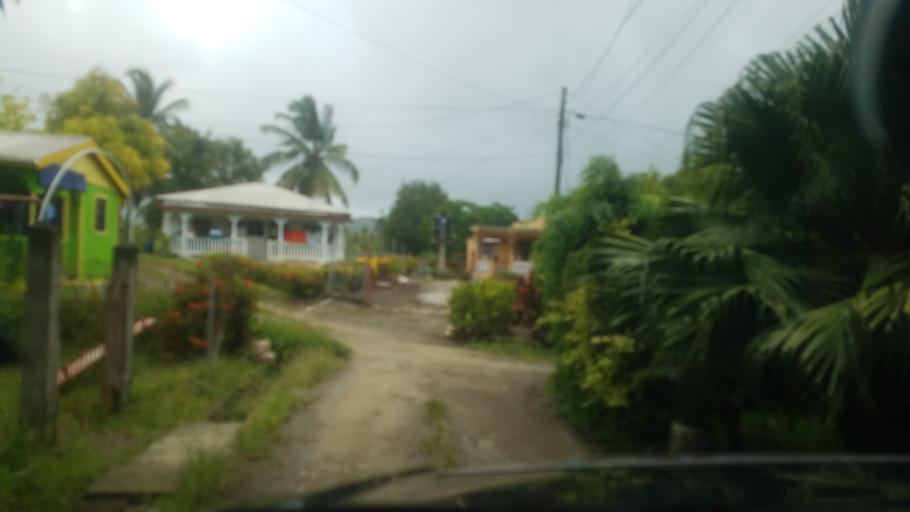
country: LC
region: Laborie Quarter
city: Laborie
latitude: 13.7609
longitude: -60.9740
